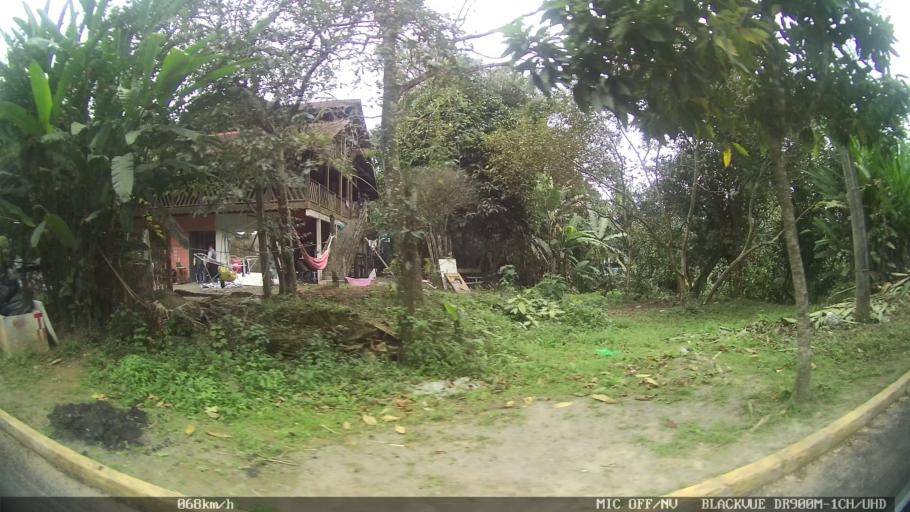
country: BR
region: Santa Catarina
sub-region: Joinville
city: Joinville
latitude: -26.3104
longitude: -48.8632
